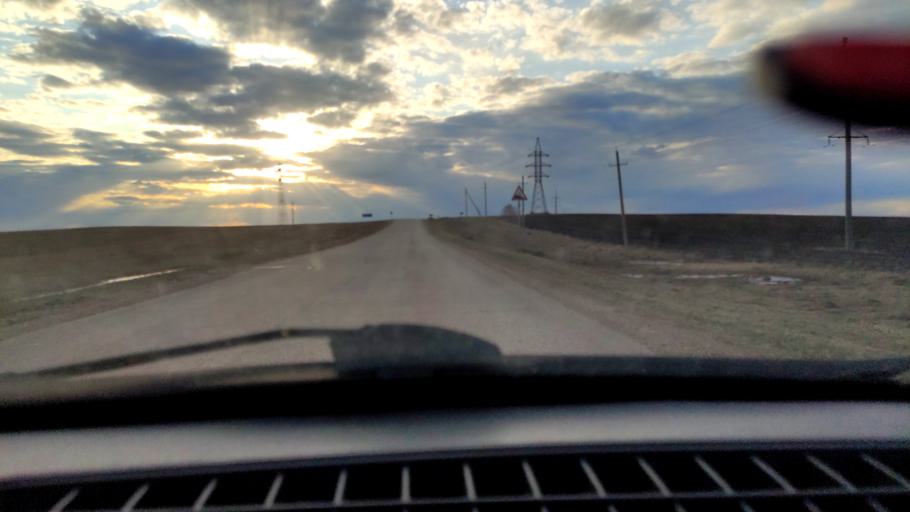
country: RU
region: Bashkortostan
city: Tolbazy
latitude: 54.0121
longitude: 55.7360
